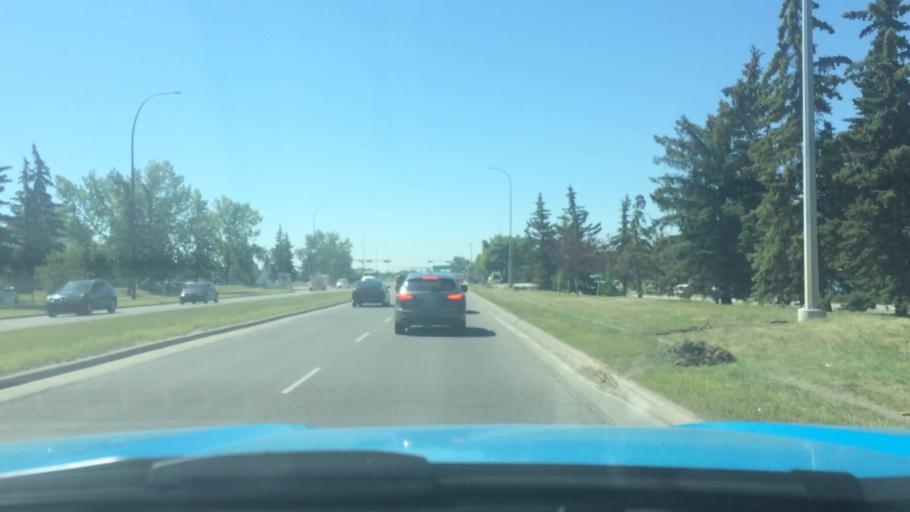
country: CA
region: Alberta
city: Calgary
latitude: 51.0735
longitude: -113.9585
